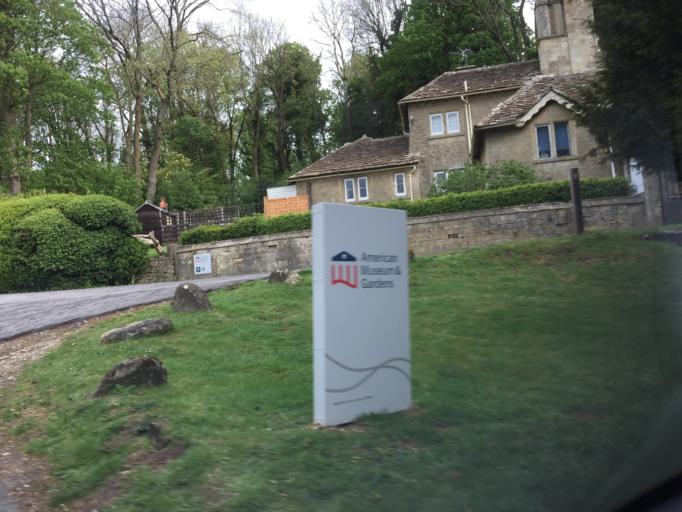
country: GB
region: England
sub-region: Bath and North East Somerset
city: Freshford
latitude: 51.3747
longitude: -2.3160
